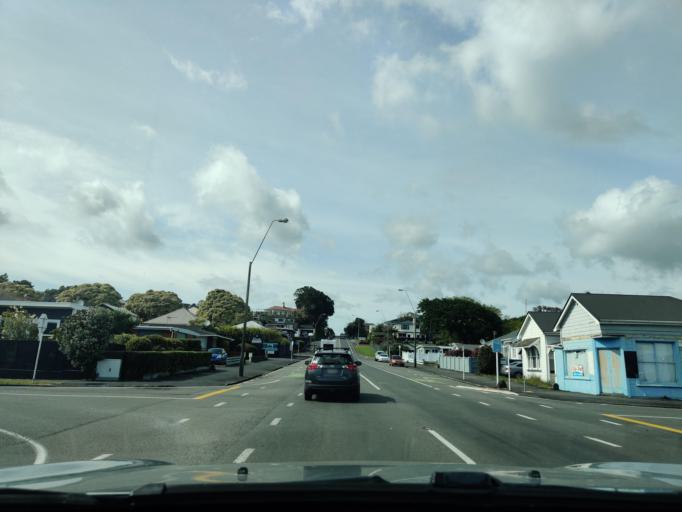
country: NZ
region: Taranaki
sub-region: New Plymouth District
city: New Plymouth
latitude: -39.0575
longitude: 174.0839
